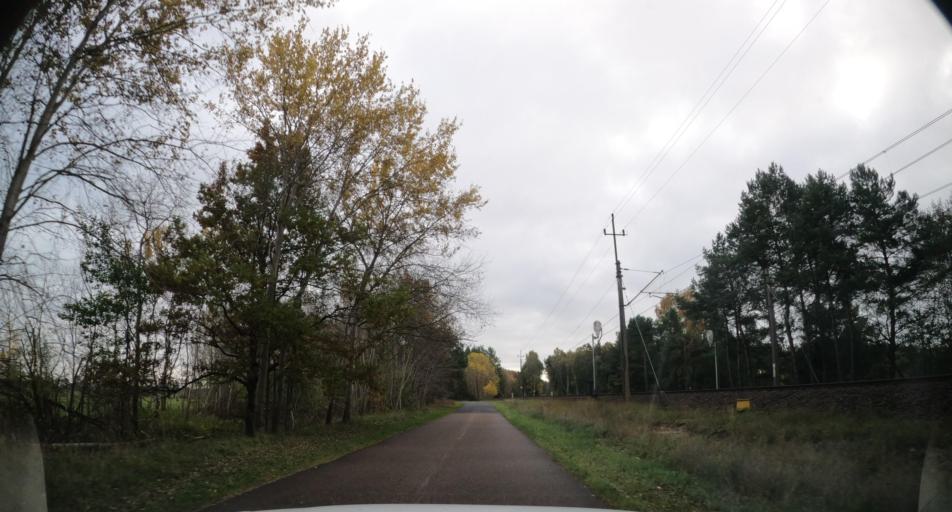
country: PL
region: West Pomeranian Voivodeship
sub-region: Powiat kamienski
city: Wolin
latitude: 53.9202
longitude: 14.5565
